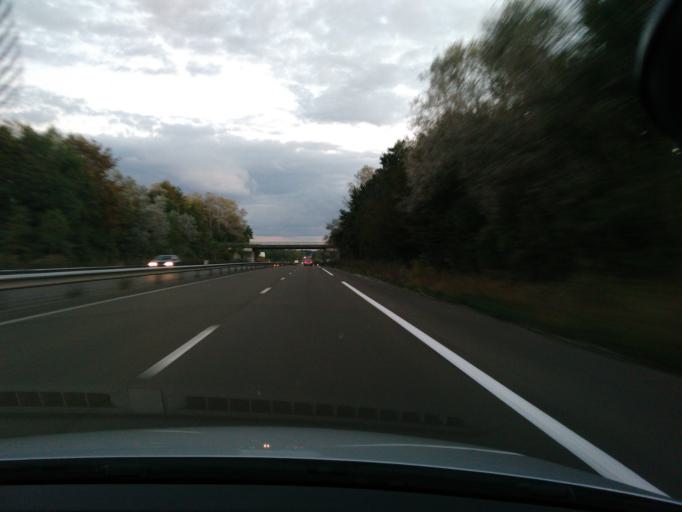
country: FR
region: Ile-de-France
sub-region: Departement de Seine-et-Marne
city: Quincy-Voisins
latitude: 48.9081
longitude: 2.8846
